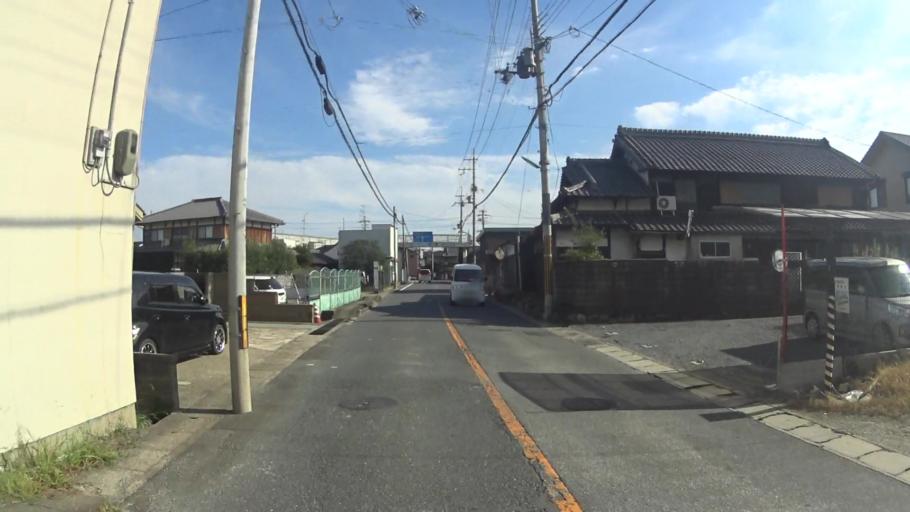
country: JP
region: Kyoto
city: Yawata
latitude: 34.8695
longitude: 135.7309
